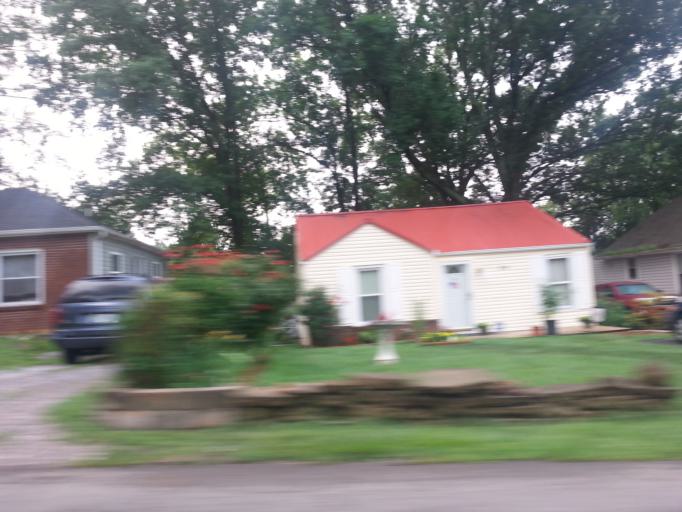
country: US
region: Tennessee
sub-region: Knox County
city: Knoxville
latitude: 35.9365
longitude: -83.9098
